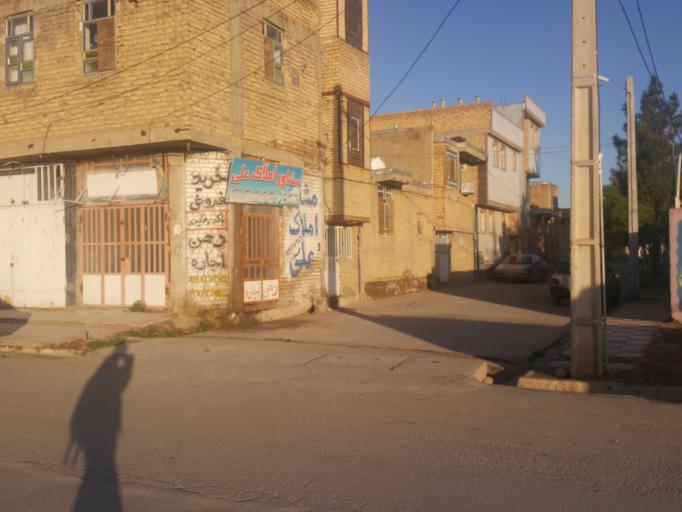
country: IR
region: Fars
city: Marvdasht
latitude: 29.8748
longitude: 52.8270
